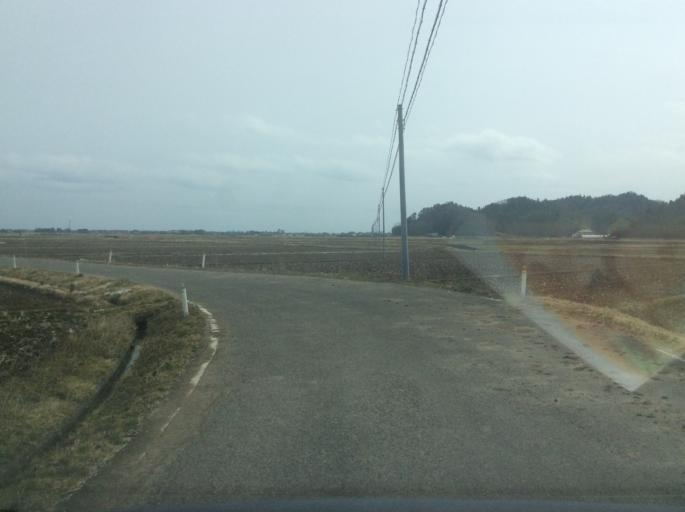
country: JP
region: Fukushima
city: Iwaki
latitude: 37.0929
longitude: 140.9430
